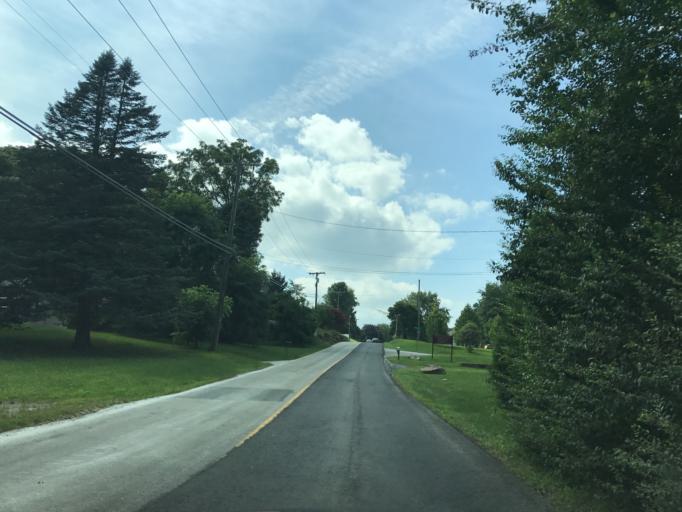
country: US
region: Maryland
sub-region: Harford County
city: South Bel Air
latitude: 39.5604
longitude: -76.3069
